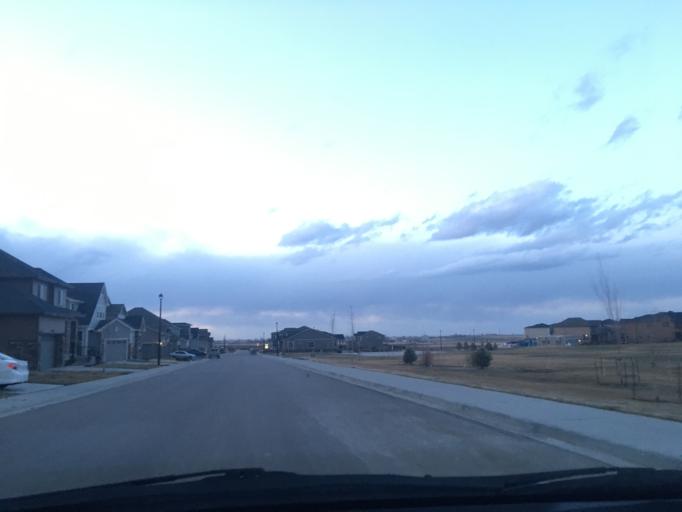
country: US
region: Colorado
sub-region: Adams County
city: Todd Creek
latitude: 39.9539
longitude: -104.9204
